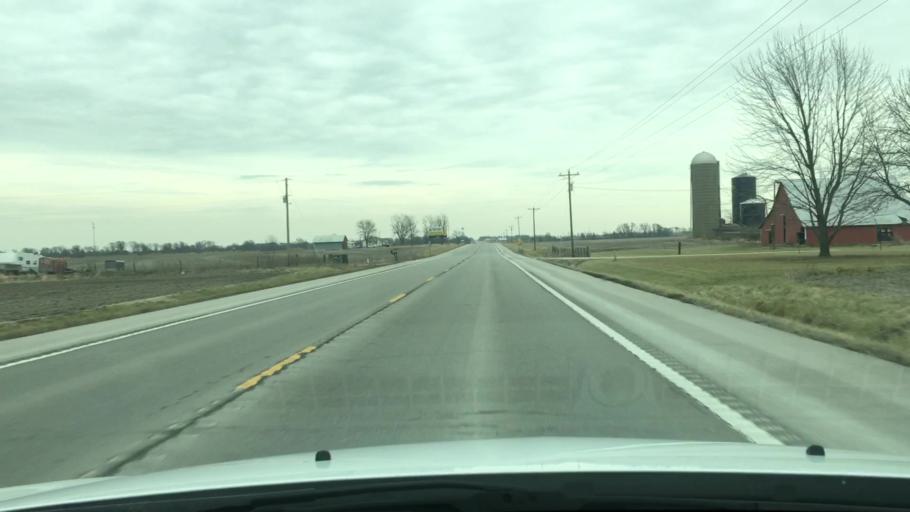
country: US
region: Missouri
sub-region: Montgomery County
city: Wellsville
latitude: 39.1635
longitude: -91.6721
